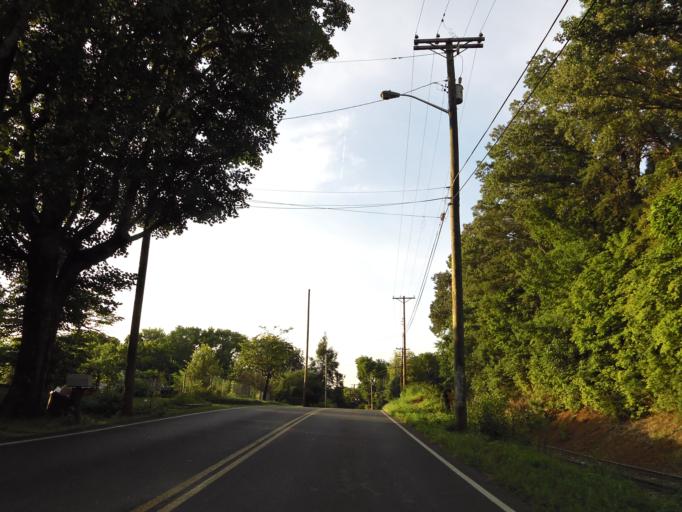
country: US
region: Tennessee
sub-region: Knox County
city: Knoxville
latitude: 35.9451
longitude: -83.9200
